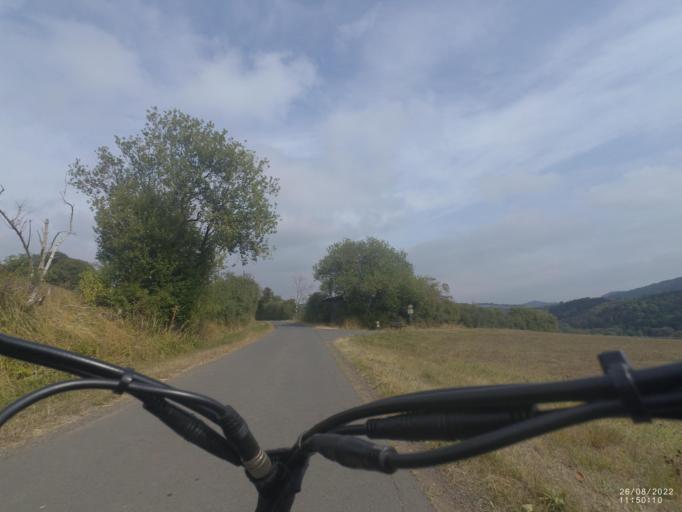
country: DE
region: Rheinland-Pfalz
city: Gerolstein
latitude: 50.2207
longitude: 6.6278
